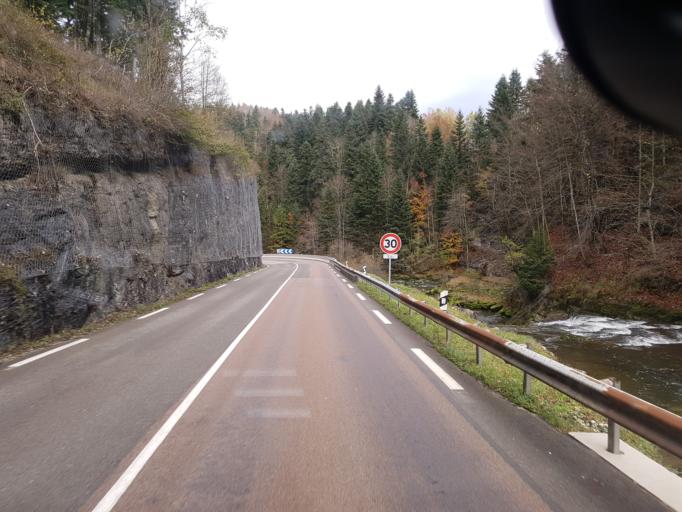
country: FR
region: Franche-Comte
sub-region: Departement du Jura
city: Champagnole
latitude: 46.6626
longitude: 5.9468
